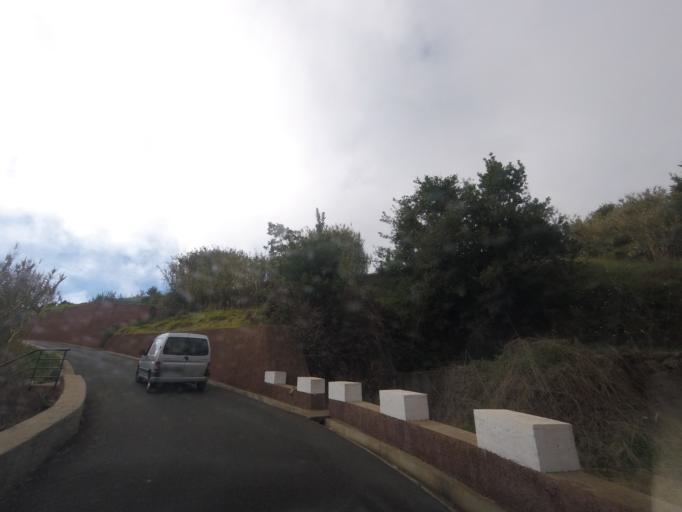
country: PT
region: Madeira
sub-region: Calheta
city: Faja da Ovelha
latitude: 32.7663
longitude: -17.2201
